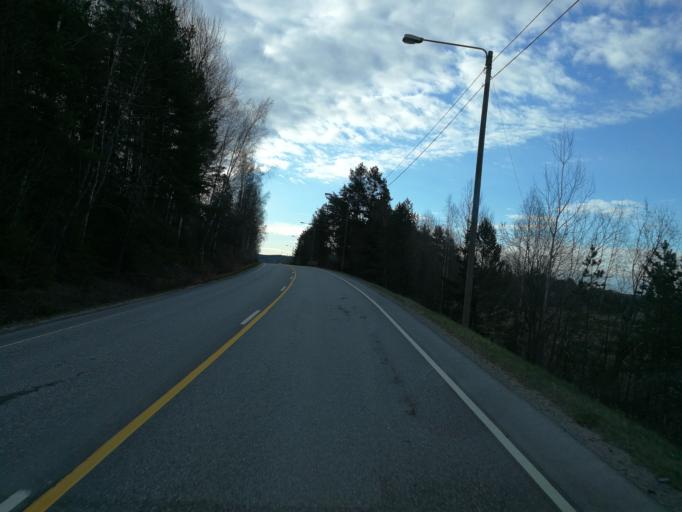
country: FI
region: Varsinais-Suomi
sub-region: Turku
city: Paimio
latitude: 60.4249
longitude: 22.6330
